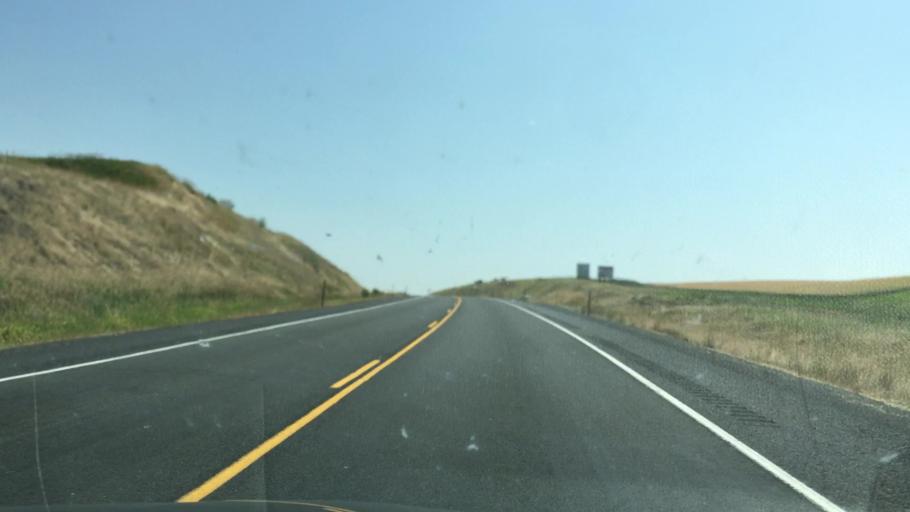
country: US
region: Idaho
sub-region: Lewis County
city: Nezperce
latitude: 46.2342
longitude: -116.5106
